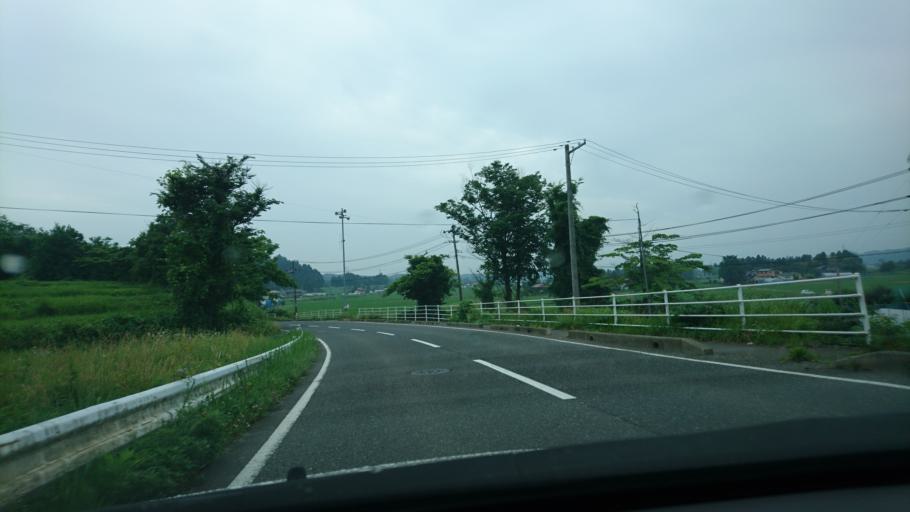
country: JP
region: Miyagi
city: Furukawa
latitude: 38.7314
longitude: 140.9905
